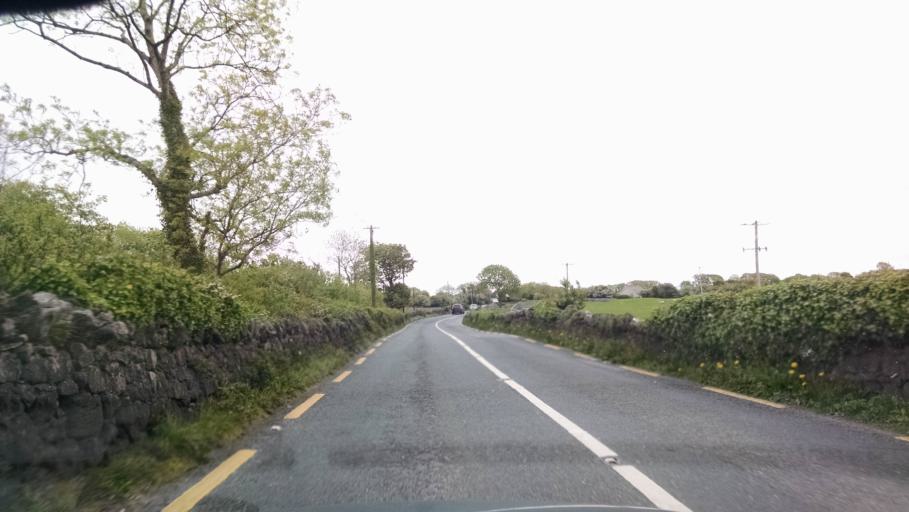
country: IE
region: Connaught
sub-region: County Galway
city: Moycullen
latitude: 53.4380
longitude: -9.0662
